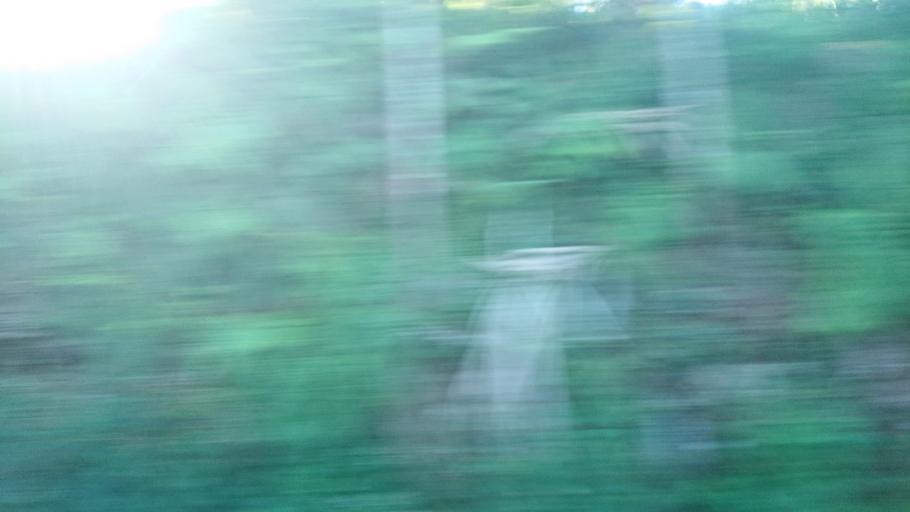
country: TW
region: Taiwan
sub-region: Chiayi
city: Jiayi Shi
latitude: 23.5369
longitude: 120.6324
